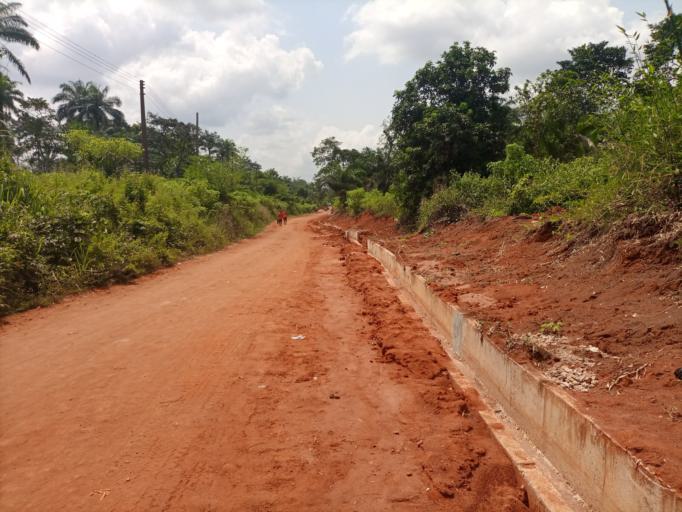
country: NG
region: Abia
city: Umuahia
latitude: 5.4813
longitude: 7.3302
